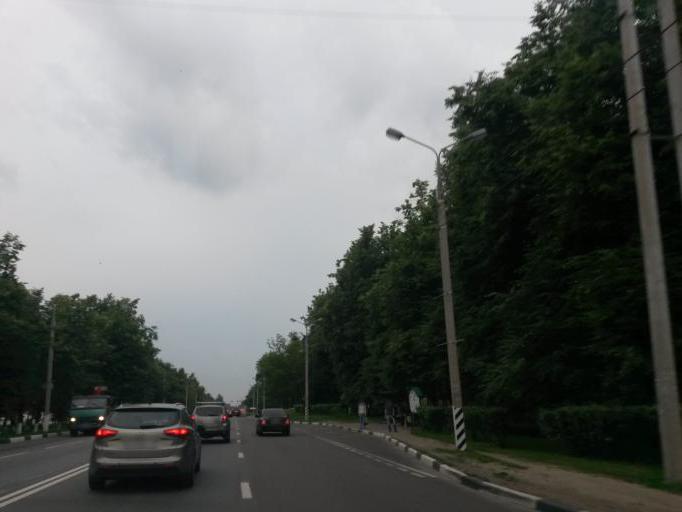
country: RU
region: Moskovskaya
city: Domodedovo
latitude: 55.4279
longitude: 37.7709
